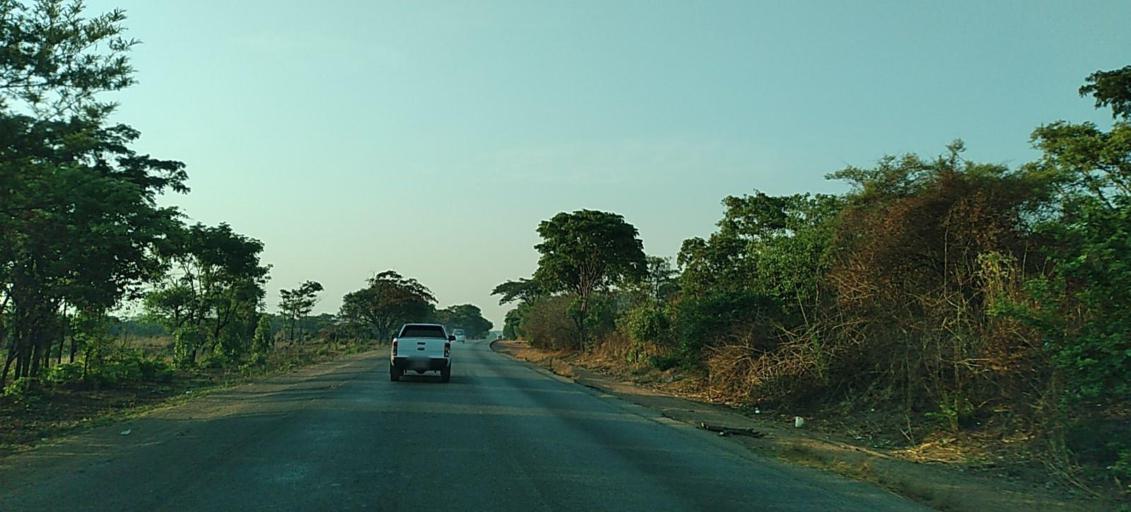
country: ZM
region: Copperbelt
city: Ndola
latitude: -13.0770
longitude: 28.7005
